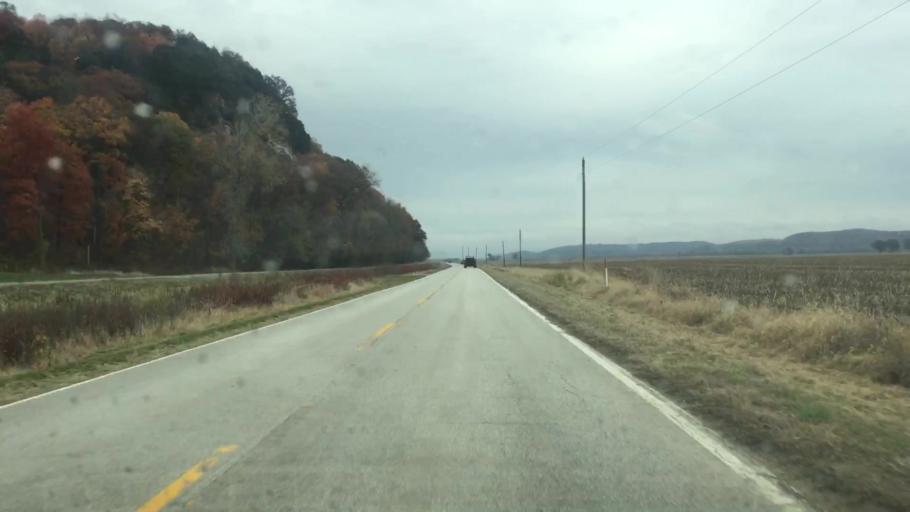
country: US
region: Missouri
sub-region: Gasconade County
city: Hermann
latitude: 38.7028
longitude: -91.5744
